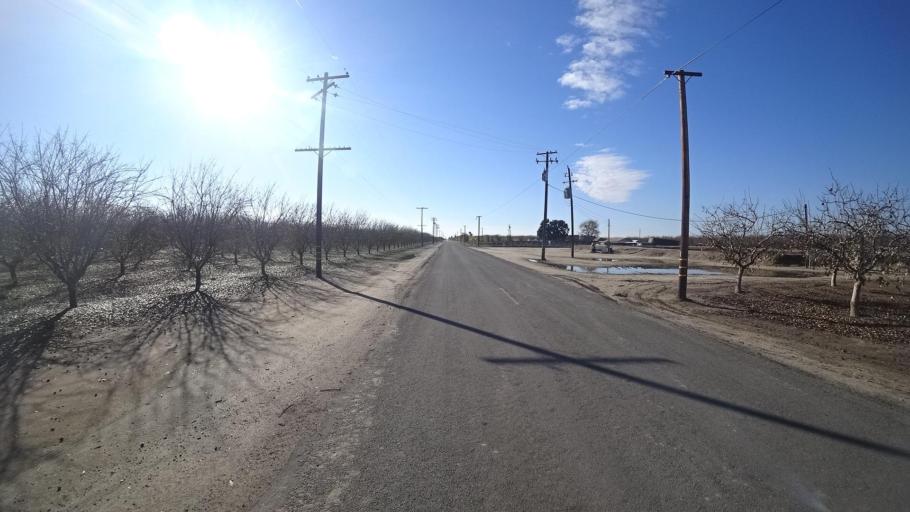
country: US
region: California
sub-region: Kern County
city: Delano
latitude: 35.7339
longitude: -119.3119
